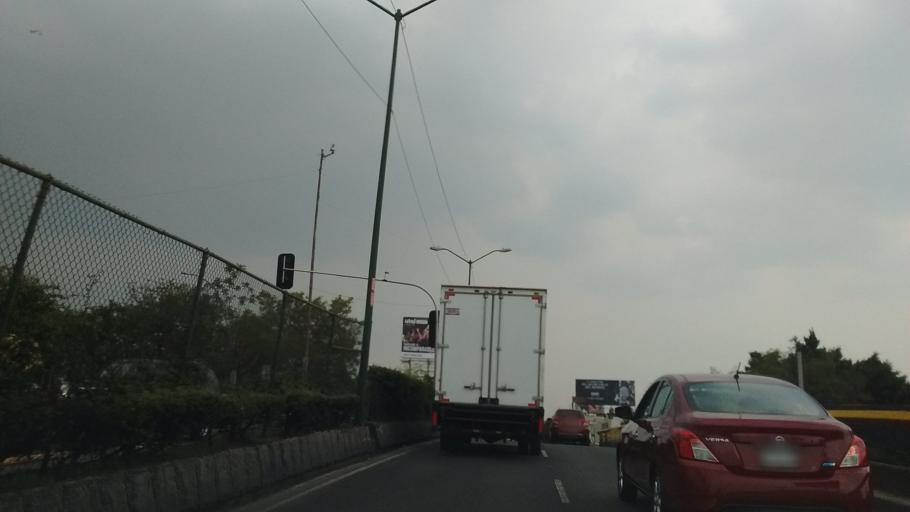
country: MX
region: Mexico City
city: Polanco
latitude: 19.4022
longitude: -99.1867
